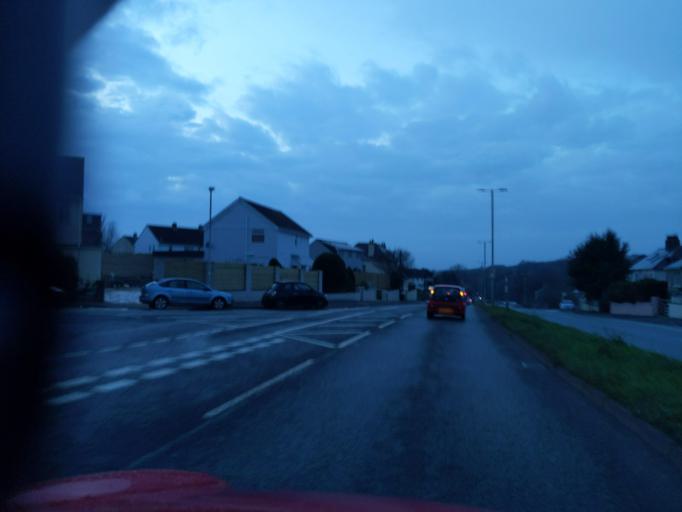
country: GB
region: England
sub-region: Plymouth
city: Plymstock
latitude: 50.3640
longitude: -4.0767
